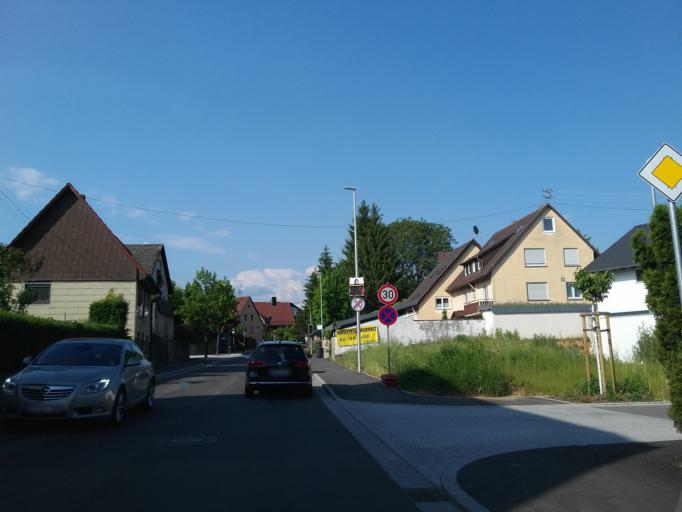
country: DE
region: Baden-Wuerttemberg
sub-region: Regierungsbezirk Stuttgart
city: Backnang
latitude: 48.9207
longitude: 9.4431
